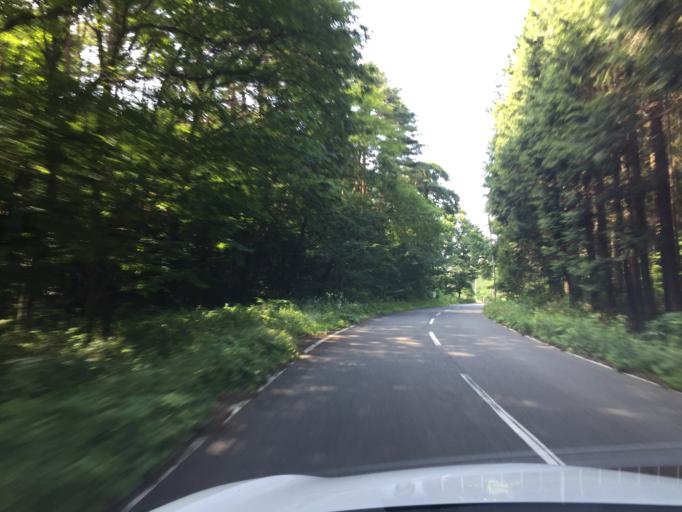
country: JP
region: Fukushima
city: Ishikawa
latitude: 37.1551
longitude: 140.6319
